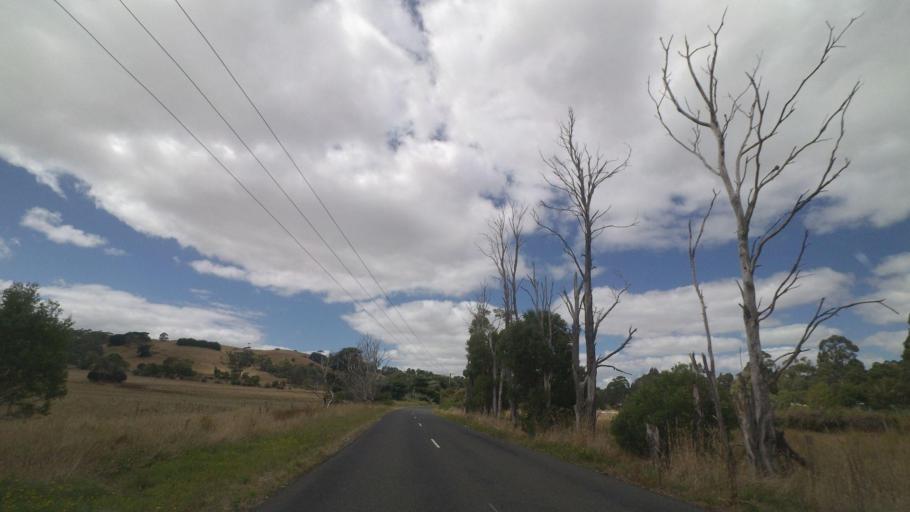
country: AU
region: Victoria
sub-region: Cardinia
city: Bunyip
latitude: -38.3443
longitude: 145.6974
